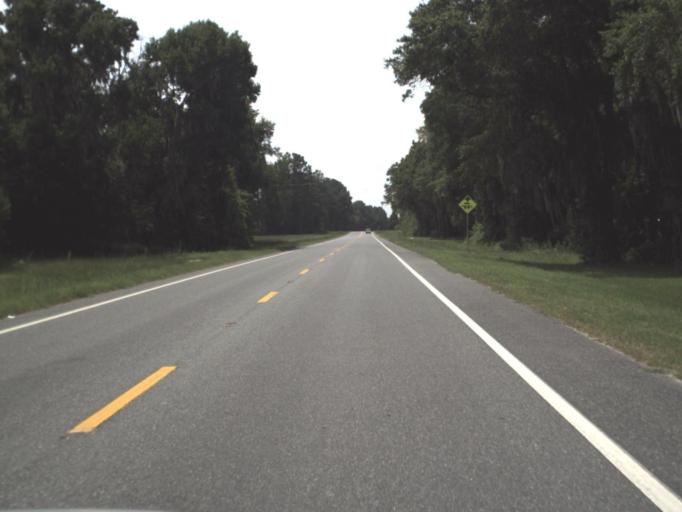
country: US
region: Florida
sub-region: Hamilton County
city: Jasper
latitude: 30.5396
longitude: -83.0504
